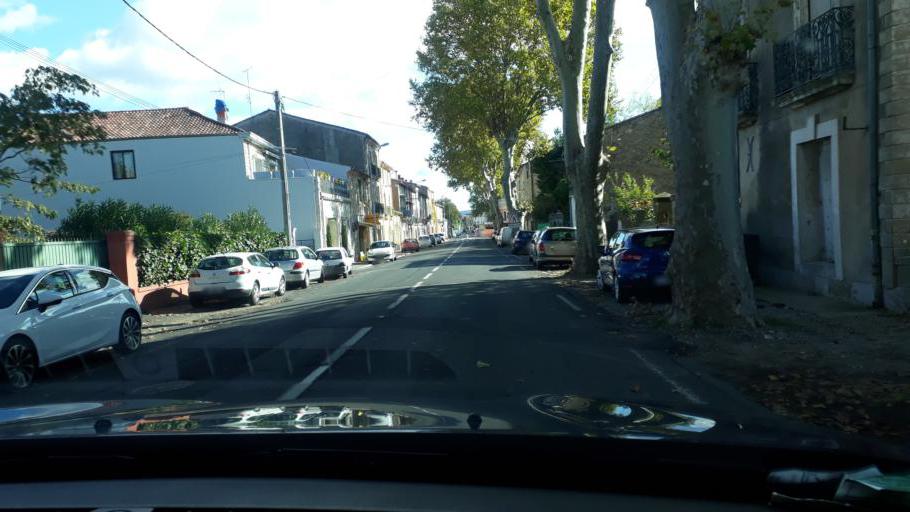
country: FR
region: Languedoc-Roussillon
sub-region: Departement de l'Herault
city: Saint-Andre-de-Sangonis
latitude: 43.6508
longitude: 3.5002
